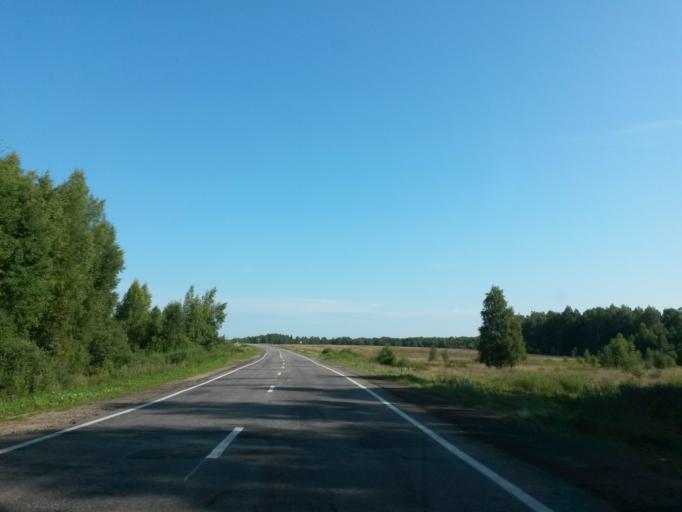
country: RU
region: Jaroslavl
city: Gavrilov-Yam
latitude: 57.3995
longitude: 39.9210
